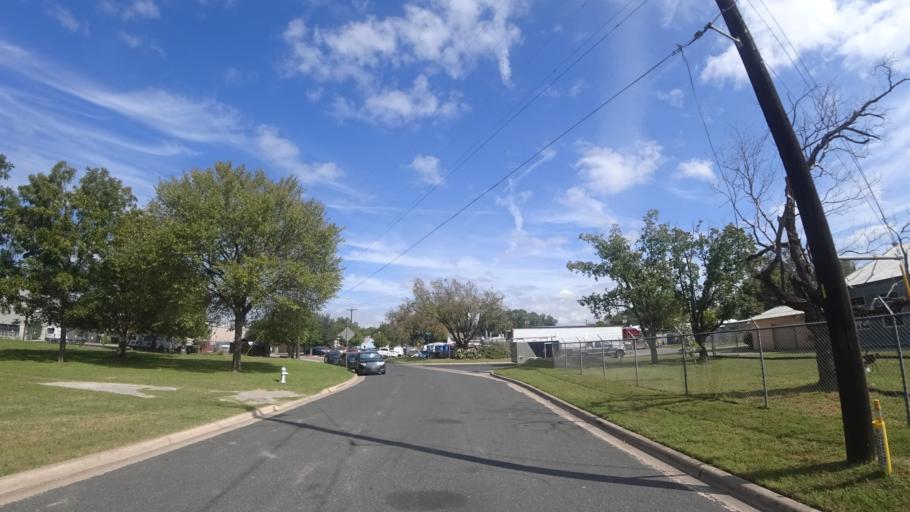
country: US
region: Texas
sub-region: Travis County
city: Austin
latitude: 30.2535
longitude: -97.7061
